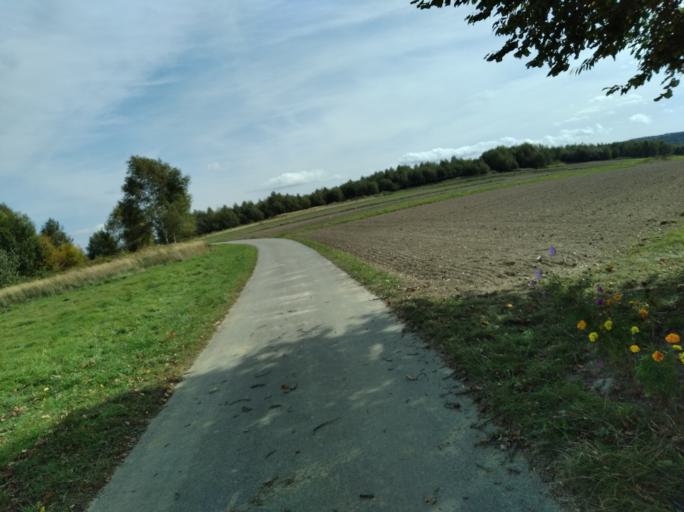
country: PL
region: Subcarpathian Voivodeship
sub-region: Powiat strzyzowski
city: Jawornik
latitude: 49.8401
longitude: 21.8745
